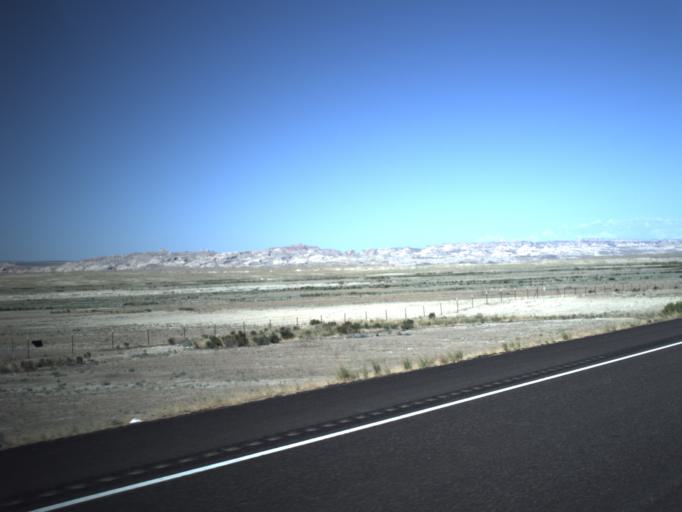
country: US
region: Utah
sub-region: Carbon County
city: East Carbon City
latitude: 39.0040
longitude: -110.2741
